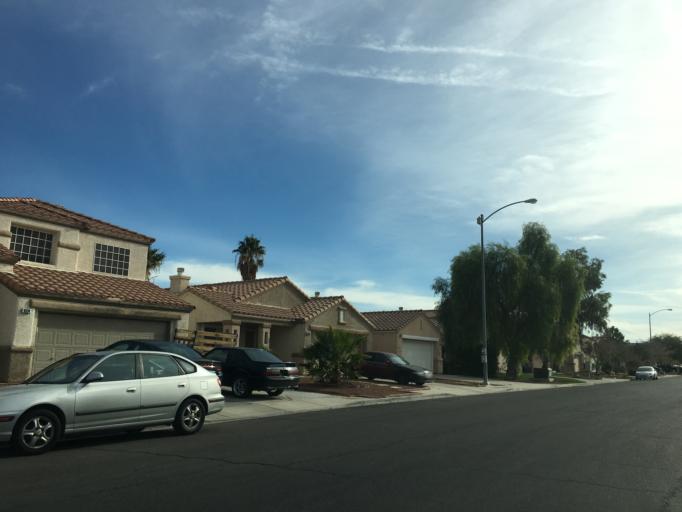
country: US
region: Nevada
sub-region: Clark County
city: Enterprise
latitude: 36.0207
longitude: -115.1650
